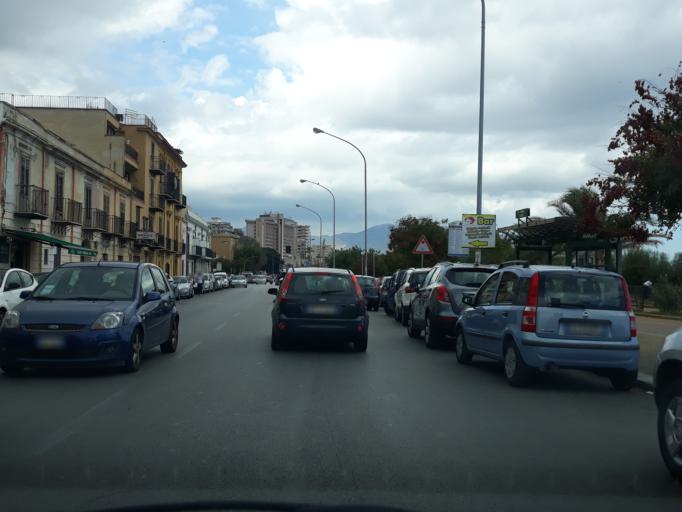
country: IT
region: Sicily
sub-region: Palermo
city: Ciaculli
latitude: 38.1058
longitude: 13.3879
